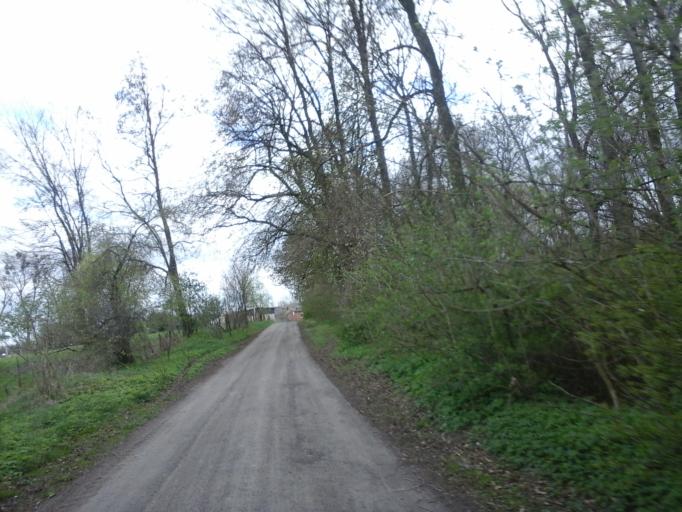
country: PL
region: West Pomeranian Voivodeship
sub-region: Powiat choszczenski
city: Bierzwnik
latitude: 53.0580
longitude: 15.5938
